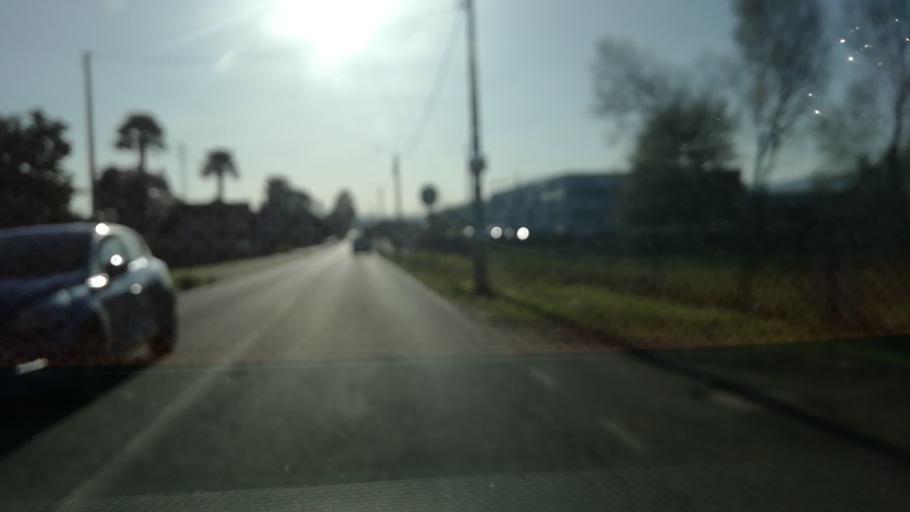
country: PT
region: Braga
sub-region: Guimaraes
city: Ponte
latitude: 41.5086
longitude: -8.3195
